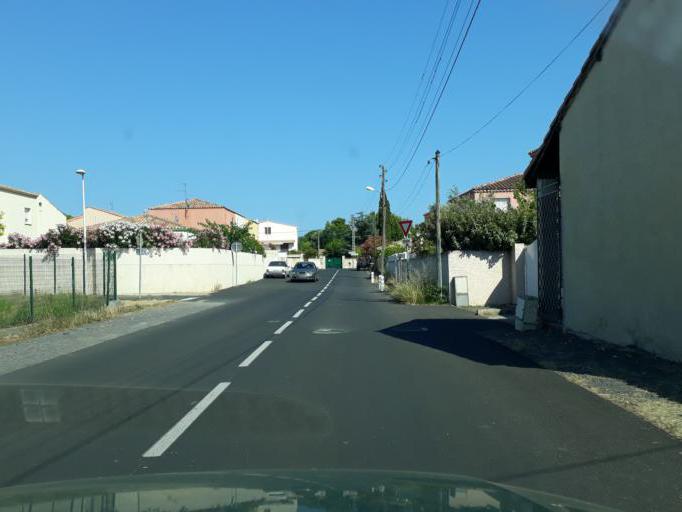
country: FR
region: Languedoc-Roussillon
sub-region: Departement de l'Herault
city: Agde
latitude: 43.2908
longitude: 3.4540
